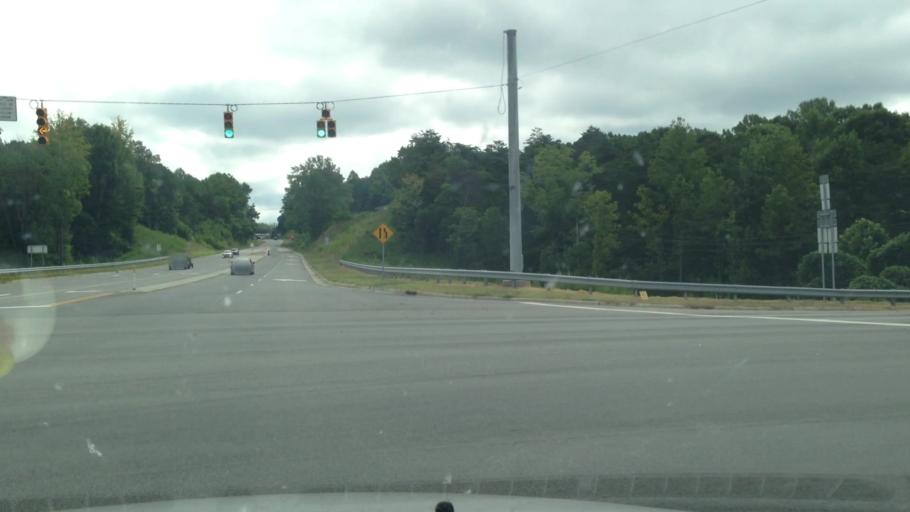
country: US
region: North Carolina
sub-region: Rockingham County
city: Reidsville
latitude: 36.3804
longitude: -79.6615
